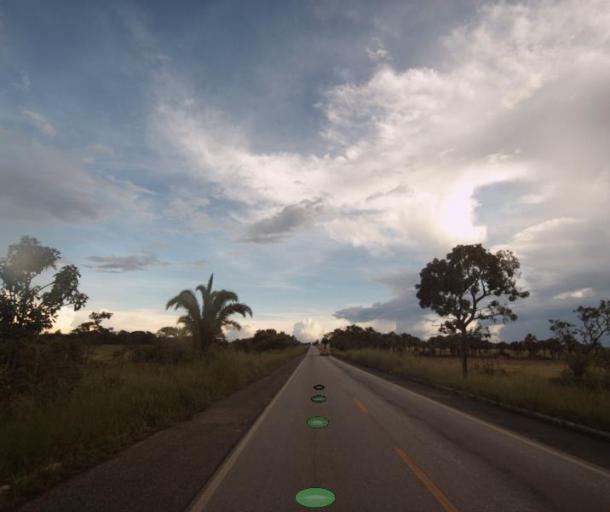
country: BR
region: Goias
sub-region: Uruacu
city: Uruacu
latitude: -14.0834
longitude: -49.0988
